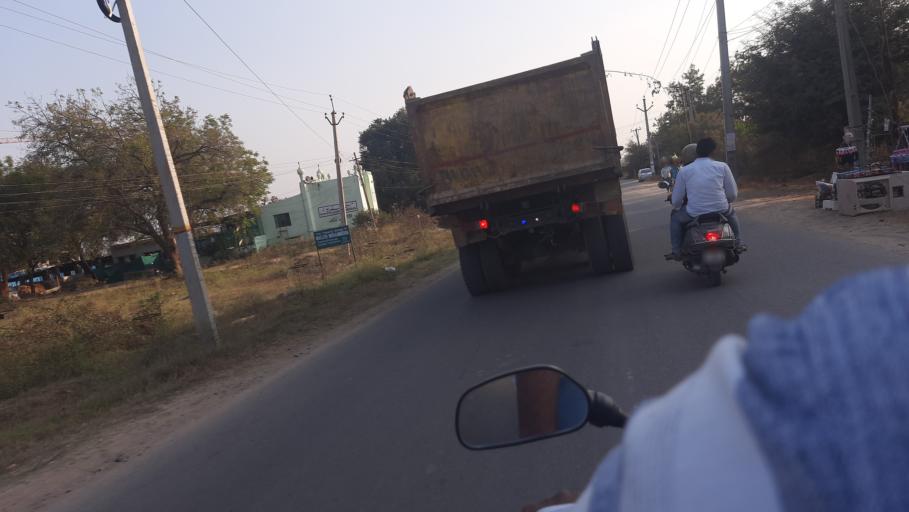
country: IN
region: Telangana
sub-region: Rangareddi
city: Secunderabad
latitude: 17.5236
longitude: 78.5416
